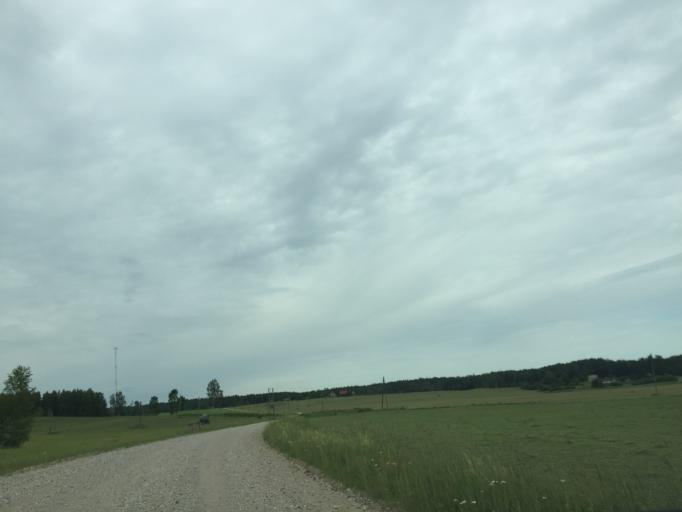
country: LV
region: Tukuma Rajons
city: Tukums
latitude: 57.0405
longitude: 23.1150
